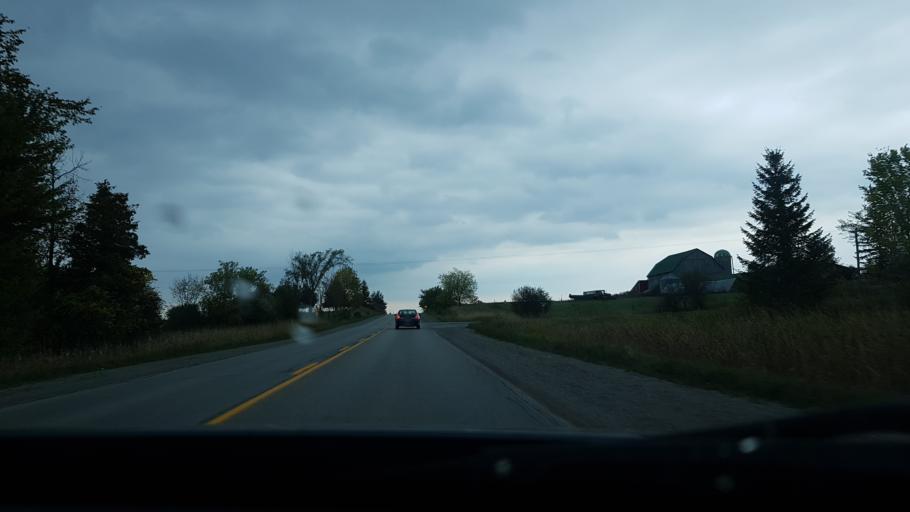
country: CA
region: Ontario
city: Omemee
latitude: 44.3708
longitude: -78.6695
